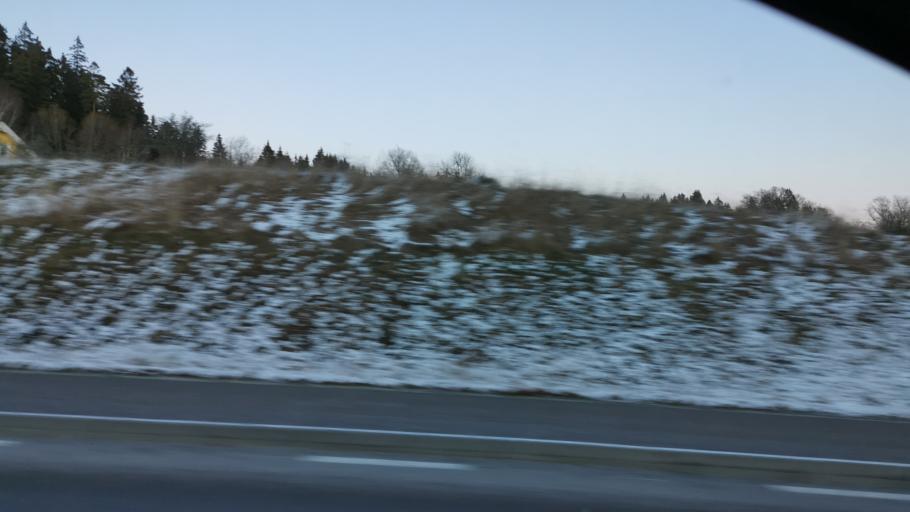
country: SE
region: Vaestra Goetaland
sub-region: Munkedals Kommun
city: Munkedal
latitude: 58.3821
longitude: 11.7735
